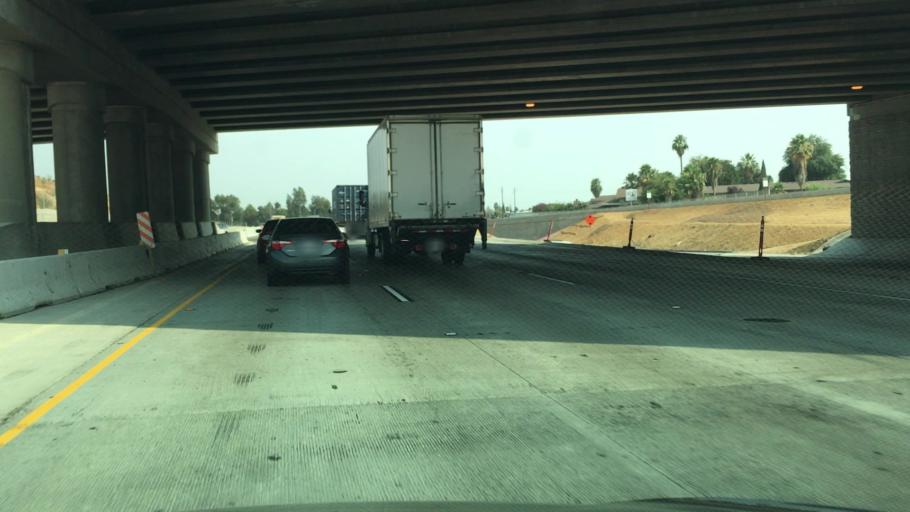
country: US
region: California
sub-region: Fresno County
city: West Park
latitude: 36.7722
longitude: -119.8389
